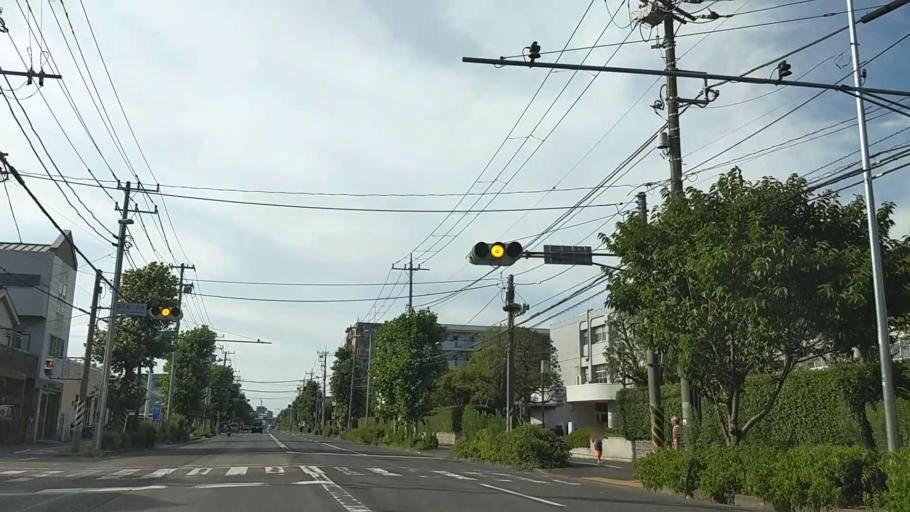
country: JP
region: Kanagawa
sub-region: Kawasaki-shi
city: Kawasaki
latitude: 35.5080
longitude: 139.6926
